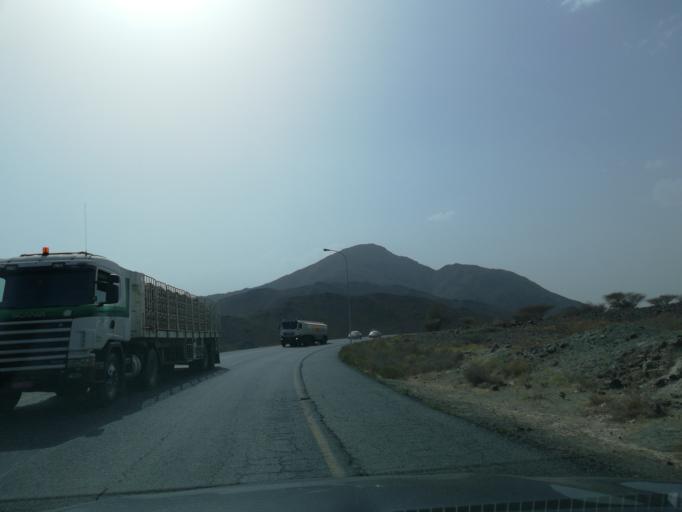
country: OM
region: Muhafazat ad Dakhiliyah
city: Sufalat Sama'il
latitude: 23.1107
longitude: 58.1558
